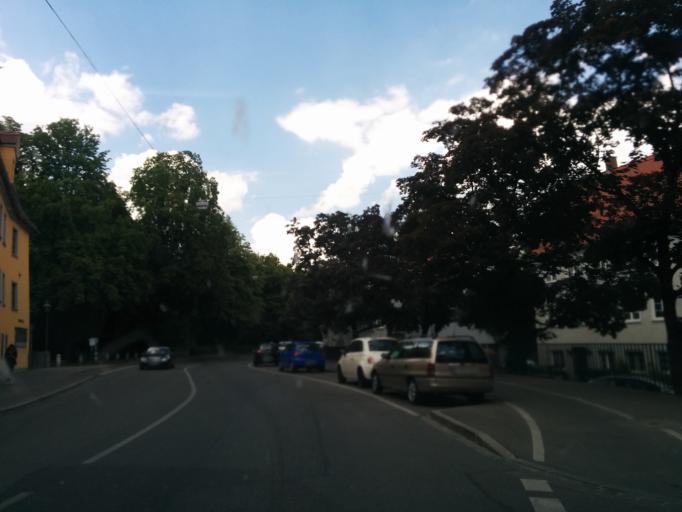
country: DE
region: Bavaria
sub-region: Swabia
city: Augsburg
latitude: 48.3718
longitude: 10.9011
